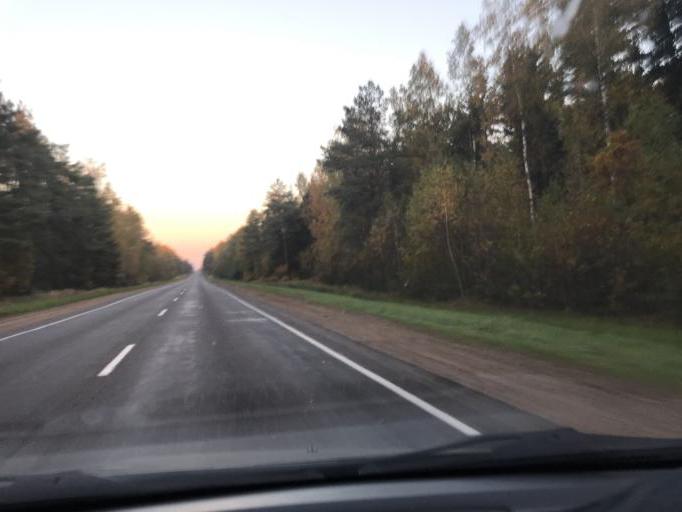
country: BY
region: Mogilev
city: Hlusha
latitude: 53.0943
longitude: 28.9593
